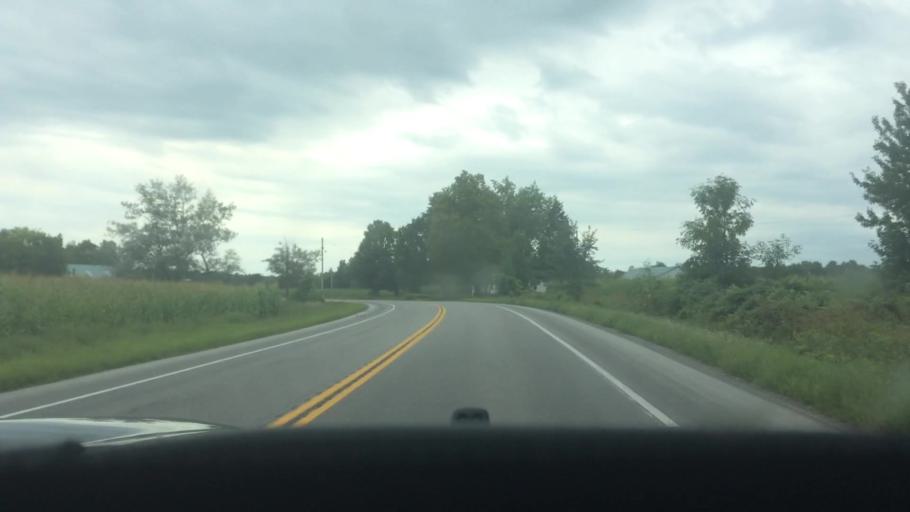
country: US
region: New York
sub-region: St. Lawrence County
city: Ogdensburg
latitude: 44.5850
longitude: -75.3713
